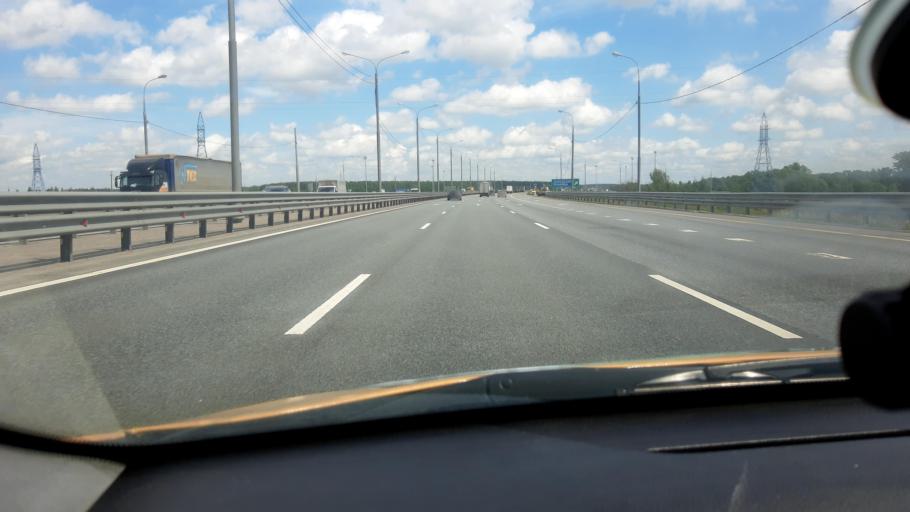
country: RU
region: Moskovskaya
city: L'vovskiy
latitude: 55.3275
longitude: 37.5618
